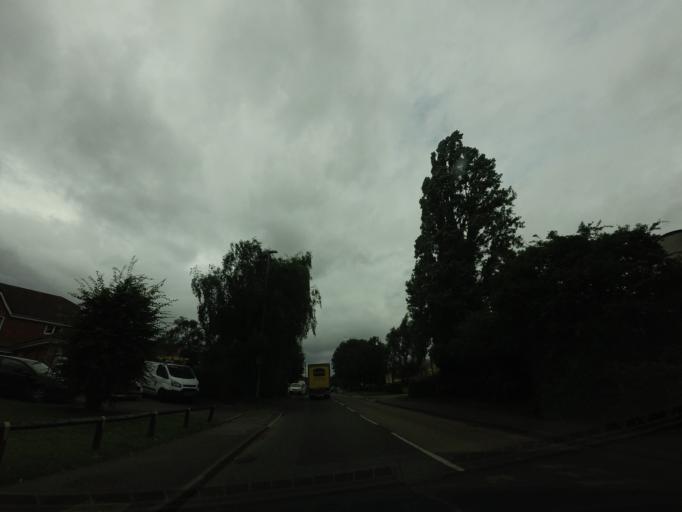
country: GB
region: England
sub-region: Nottinghamshire
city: Kimberley
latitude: 53.0010
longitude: -1.2465
